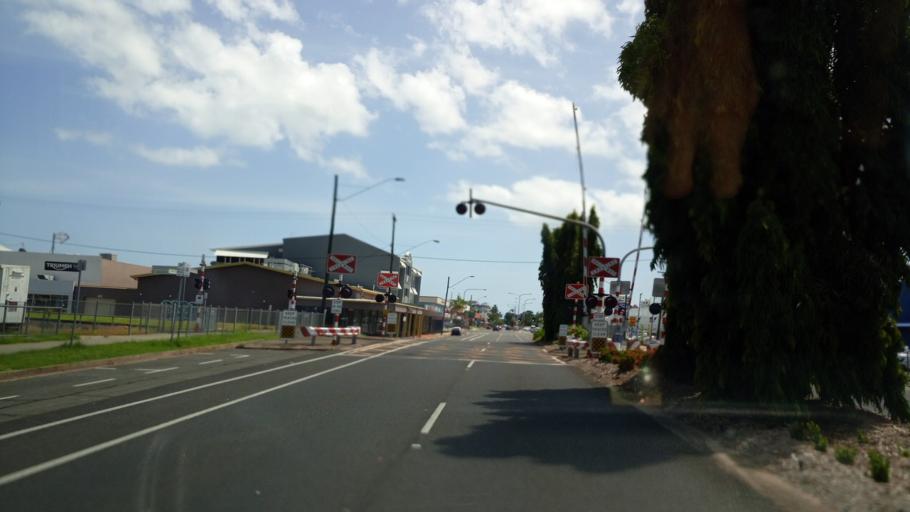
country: AU
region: Queensland
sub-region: Cairns
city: Cairns
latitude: -16.9222
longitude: 145.7683
